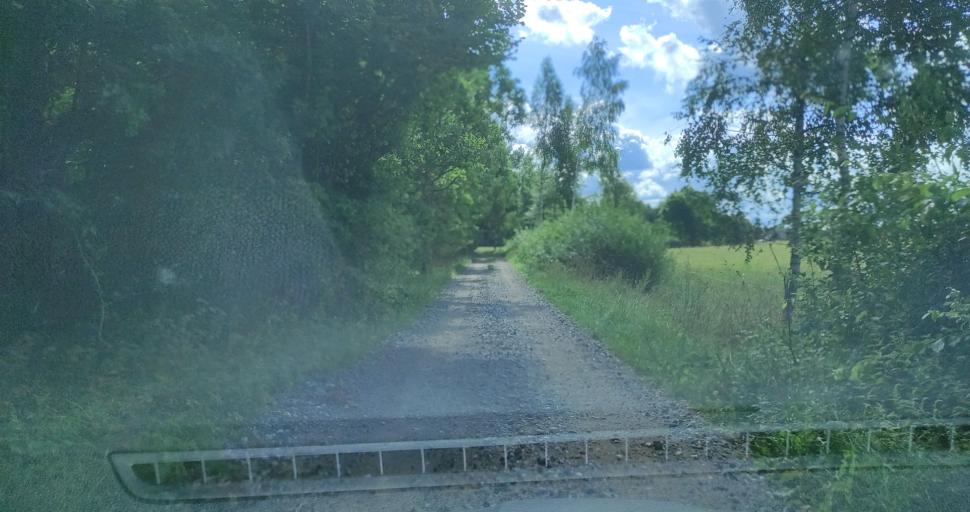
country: LV
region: Alsunga
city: Alsunga
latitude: 57.0269
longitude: 21.7016
